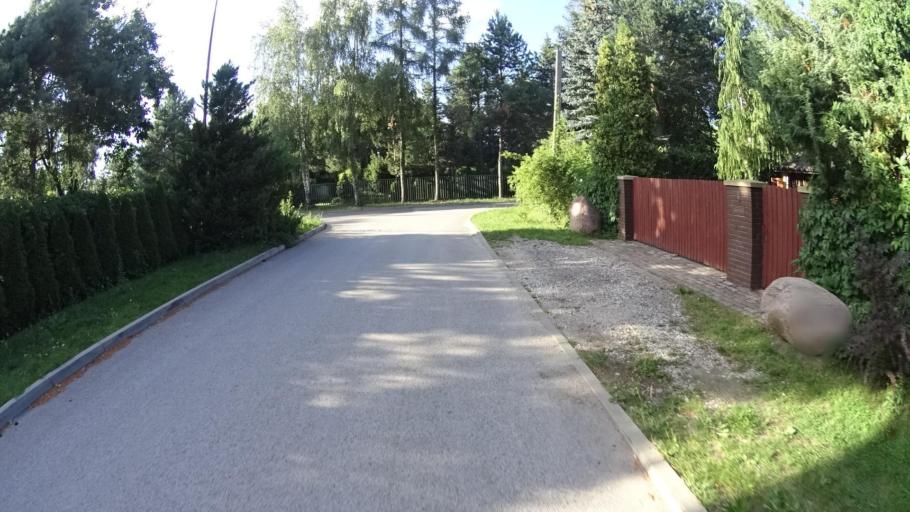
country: PL
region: Masovian Voivodeship
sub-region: Powiat piaseczynski
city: Piaseczno
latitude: 52.0678
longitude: 20.9920
